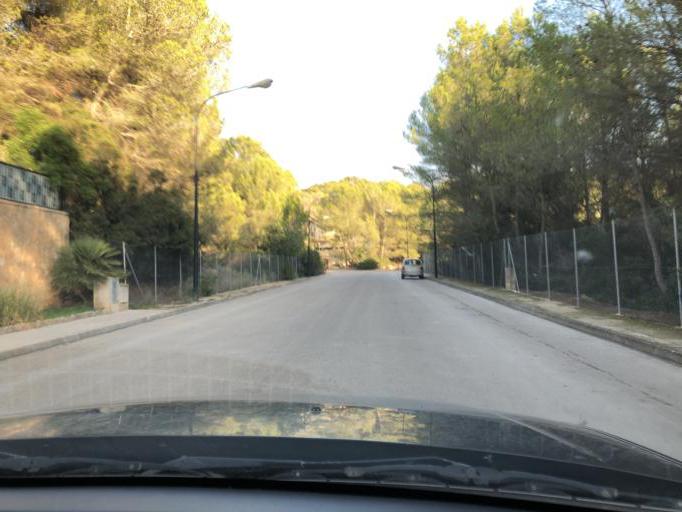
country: ES
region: Balearic Islands
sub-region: Illes Balears
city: Santa Ponsa
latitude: 39.5325
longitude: 2.4626
